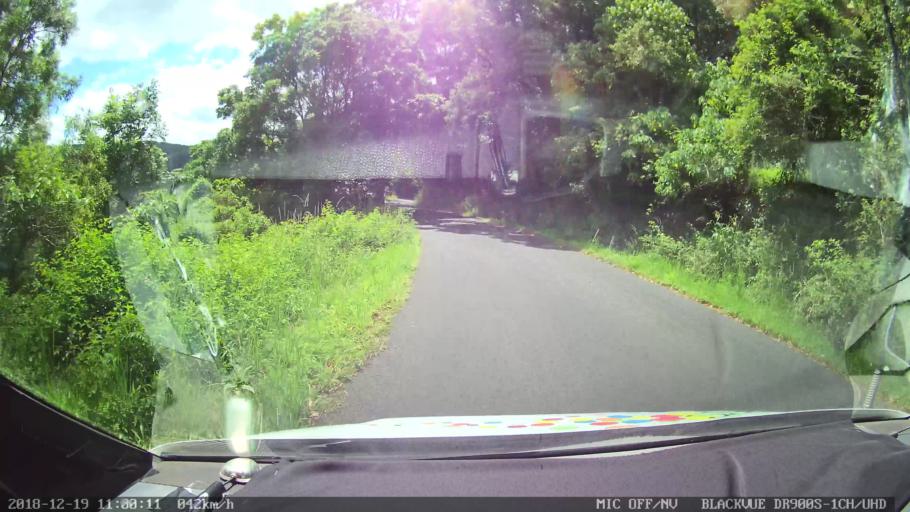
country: AU
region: New South Wales
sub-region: Lismore Municipality
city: Nimbin
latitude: -28.6008
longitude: 153.2638
